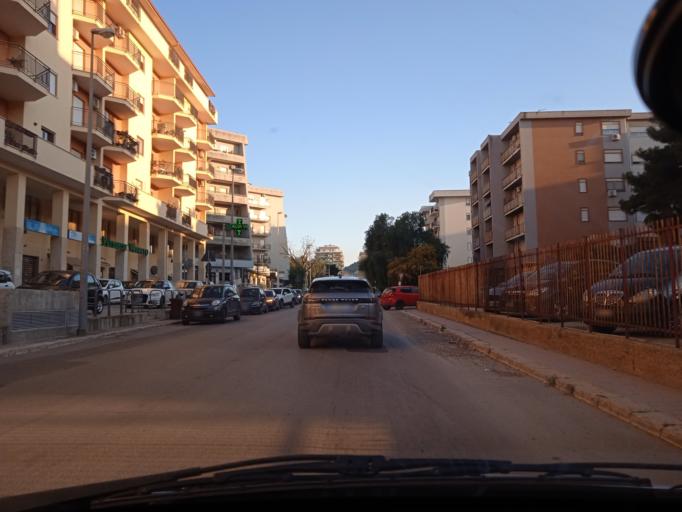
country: IT
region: Sicily
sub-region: Palermo
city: Bagheria
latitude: 38.0835
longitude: 13.5014
